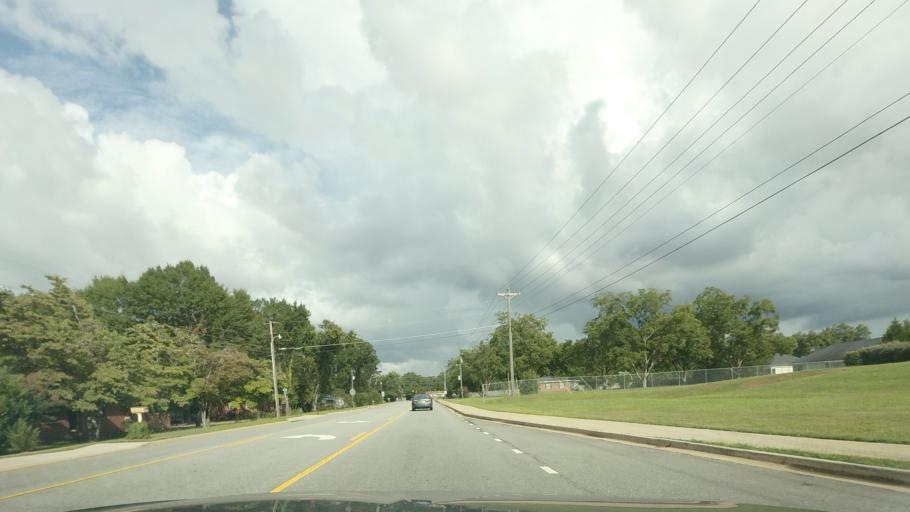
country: US
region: Georgia
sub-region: Houston County
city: Centerville
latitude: 32.6348
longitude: -83.6928
